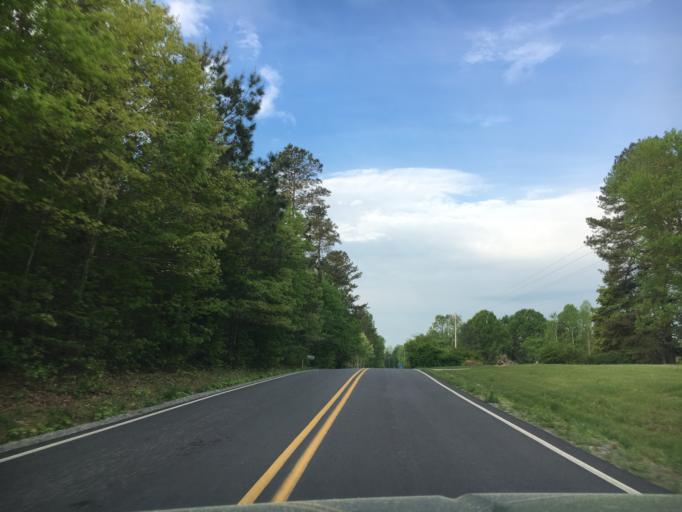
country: US
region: Virginia
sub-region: Halifax County
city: Halifax
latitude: 36.8924
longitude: -78.8319
